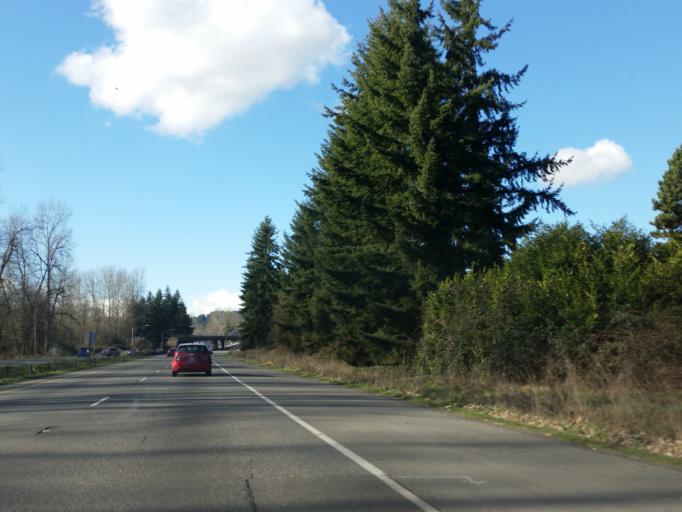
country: US
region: Washington
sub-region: Pierce County
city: Sumner
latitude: 47.1959
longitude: -122.2448
